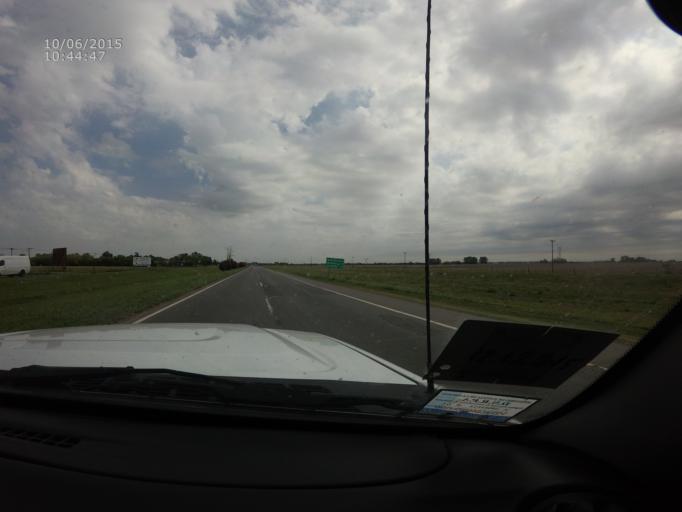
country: AR
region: Buenos Aires
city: San Nicolas de los Arroyos
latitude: -33.4418
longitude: -60.1662
